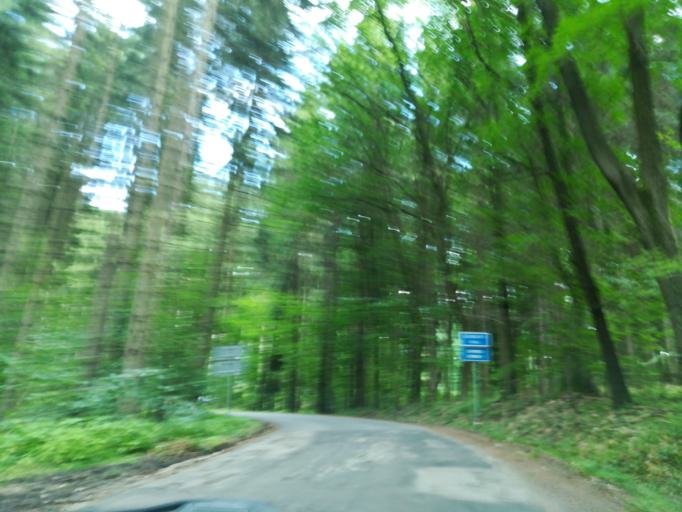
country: CZ
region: Kralovehradecky
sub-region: Okres Jicin
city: Zeleznice
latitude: 50.4824
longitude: 15.4170
